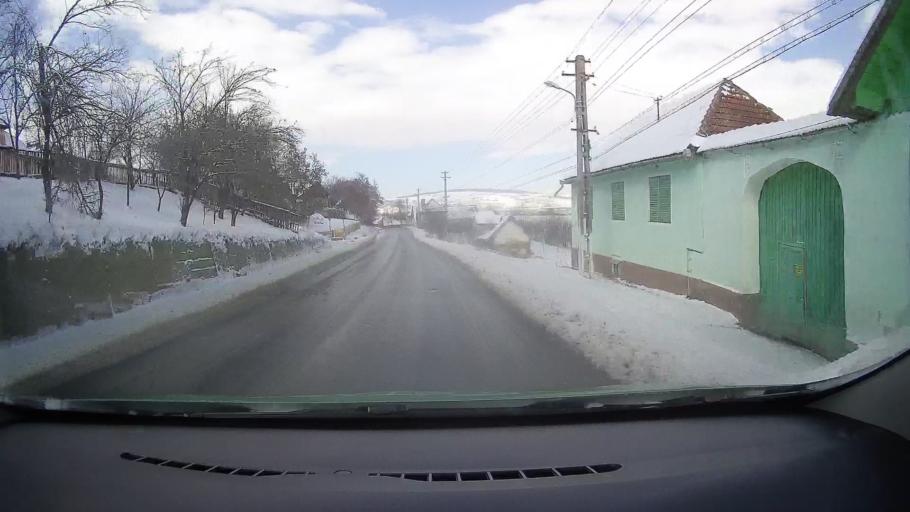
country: RO
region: Sibiu
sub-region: Comuna Altina
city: Altina
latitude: 45.9333
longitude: 24.4642
